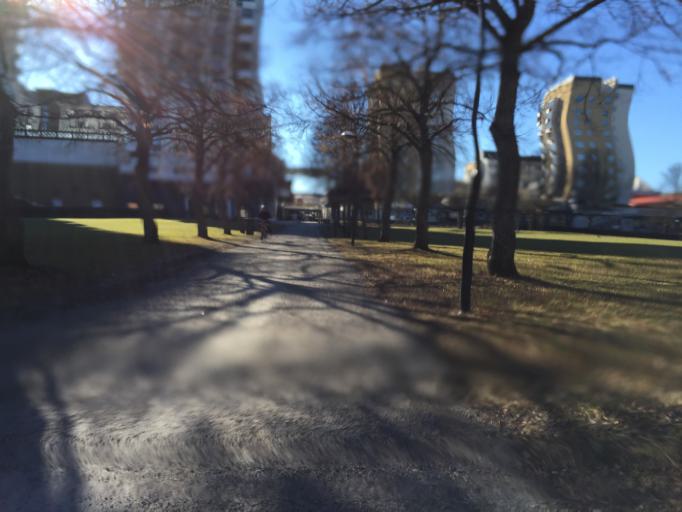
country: SE
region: Stockholm
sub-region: Stockholms Kommun
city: Bromma
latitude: 59.3646
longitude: 17.8763
